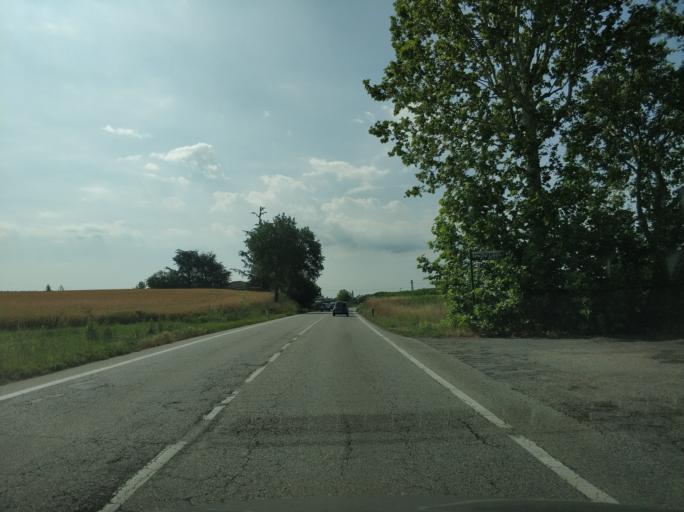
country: IT
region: Piedmont
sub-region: Provincia di Torino
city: Marocchi
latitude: 44.9355
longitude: 7.8285
